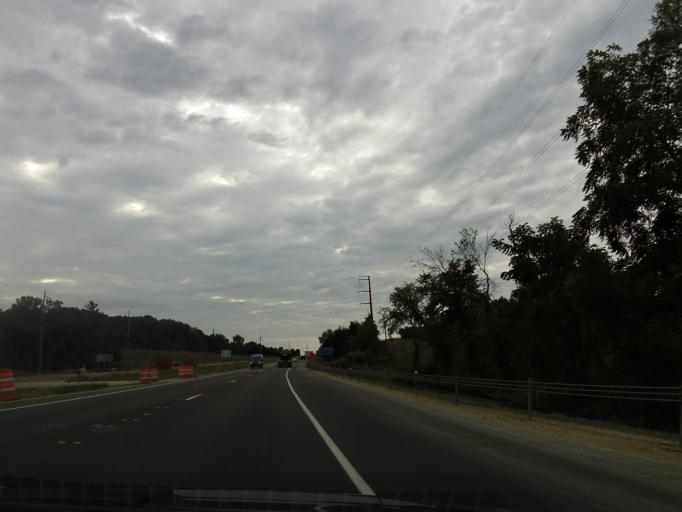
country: US
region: Minnesota
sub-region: Goodhue County
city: Cannon Falls
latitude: 44.5024
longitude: -92.9137
